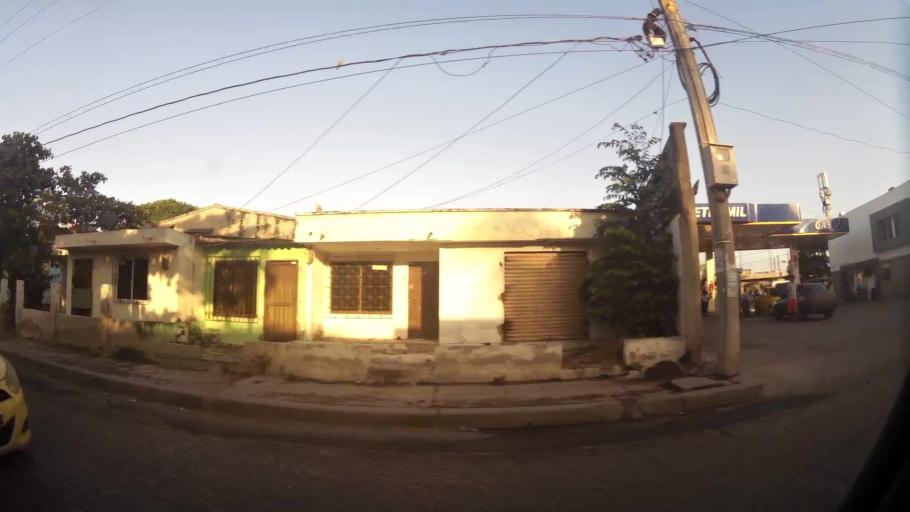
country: CO
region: Bolivar
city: Cartagena
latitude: 10.4350
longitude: -75.5288
